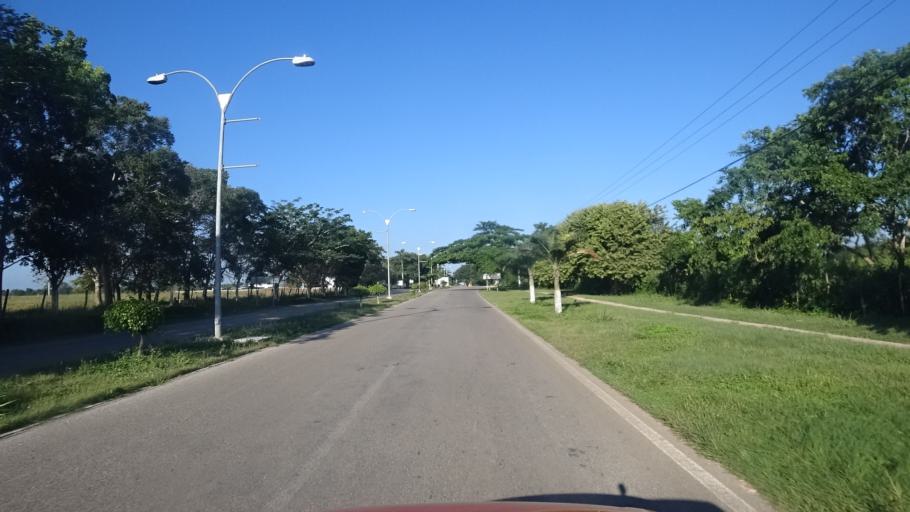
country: MX
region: Yucatan
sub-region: Tizimin
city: Tizimin
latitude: 21.1518
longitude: -88.1765
